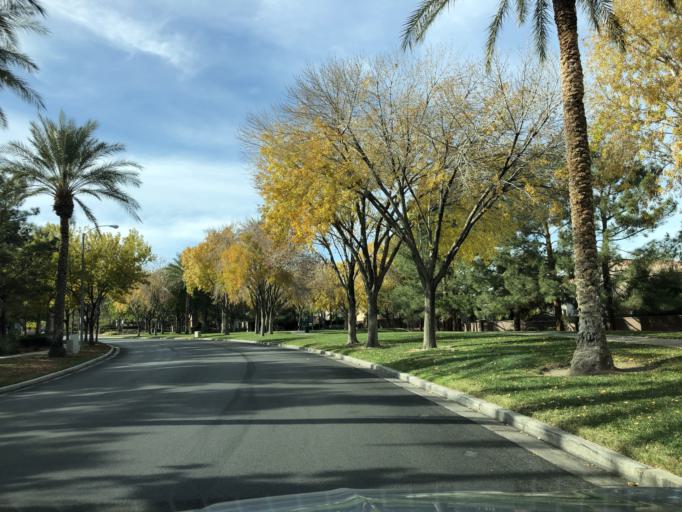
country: US
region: Nevada
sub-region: Clark County
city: Whitney
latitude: 36.0149
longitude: -115.0857
